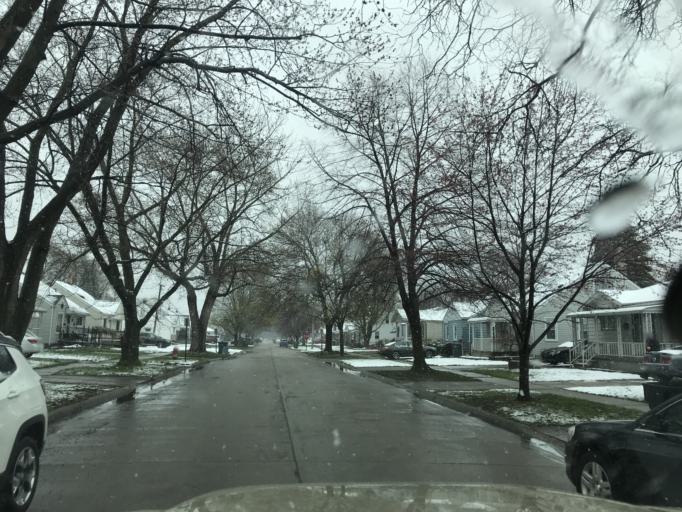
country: US
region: Michigan
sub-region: Wayne County
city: Lincoln Park
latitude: 42.2632
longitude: -83.1918
